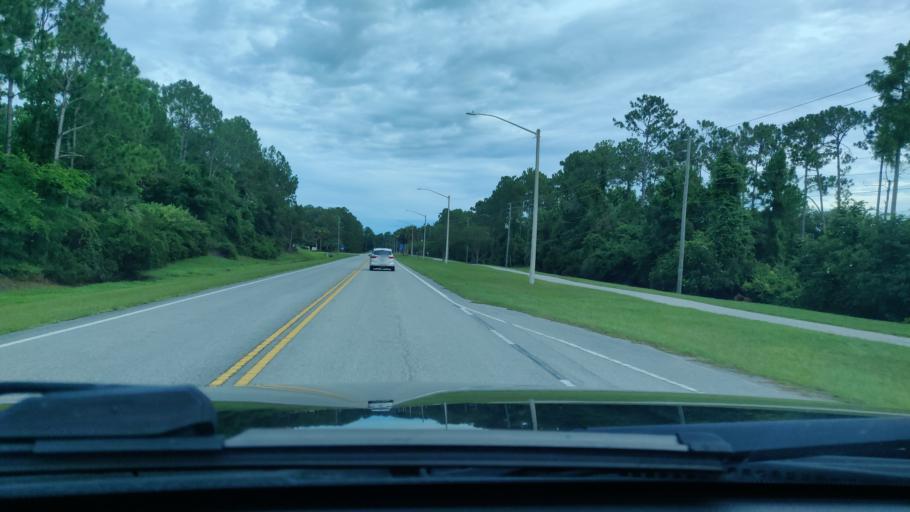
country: US
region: Florida
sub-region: Flagler County
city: Palm Coast
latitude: 29.5410
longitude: -81.2551
